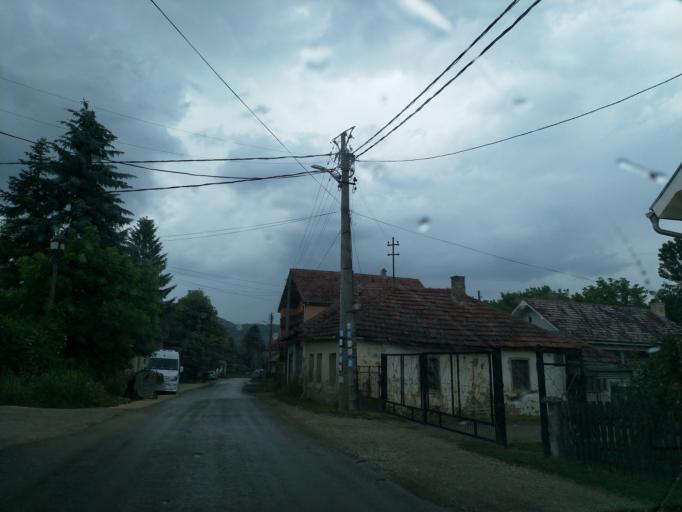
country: RS
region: Central Serbia
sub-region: Borski Okrug
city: Bor
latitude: 44.0108
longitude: 21.9845
